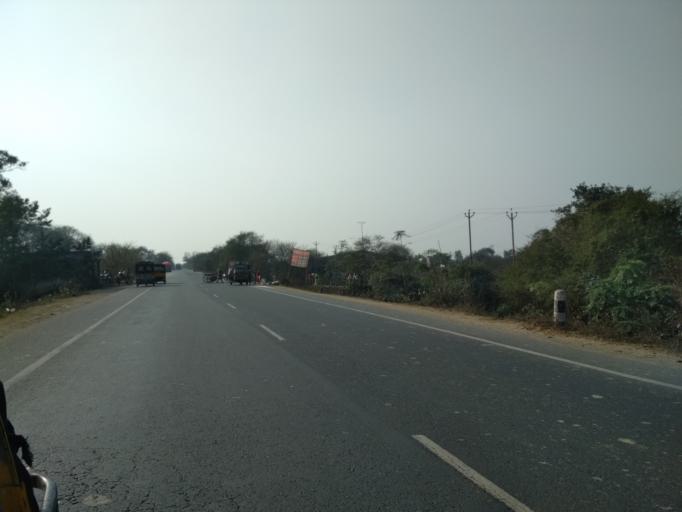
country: IN
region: Bihar
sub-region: Khagaria
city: Khagaria
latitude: 25.5074
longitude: 86.5509
